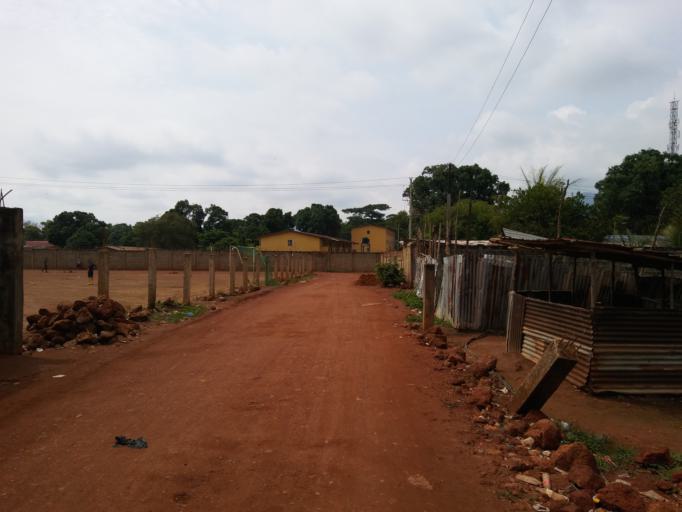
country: SL
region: Western Area
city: Hastings
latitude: 8.3877
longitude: -13.1458
